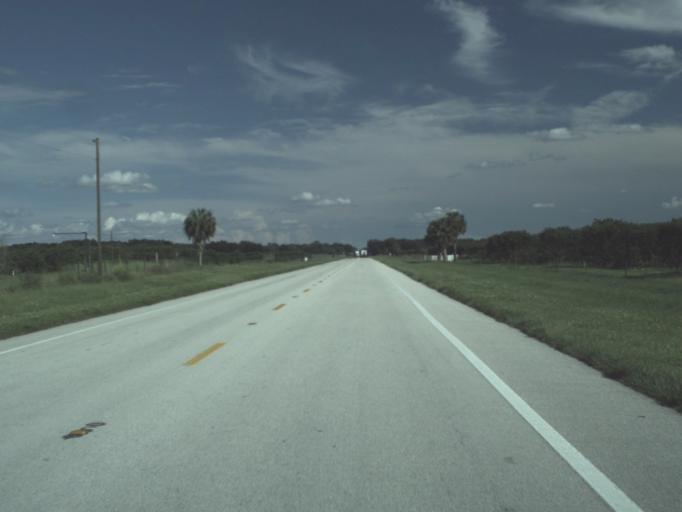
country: US
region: Florida
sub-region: Highlands County
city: Sebring
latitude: 27.4202
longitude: -81.5718
